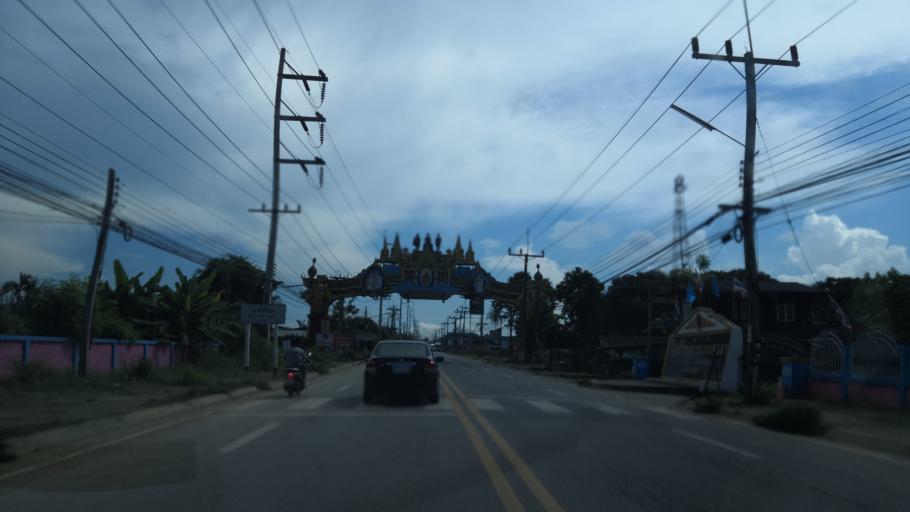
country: TH
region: Chiang Rai
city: Wiang Pa Pao
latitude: 19.3733
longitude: 99.5026
